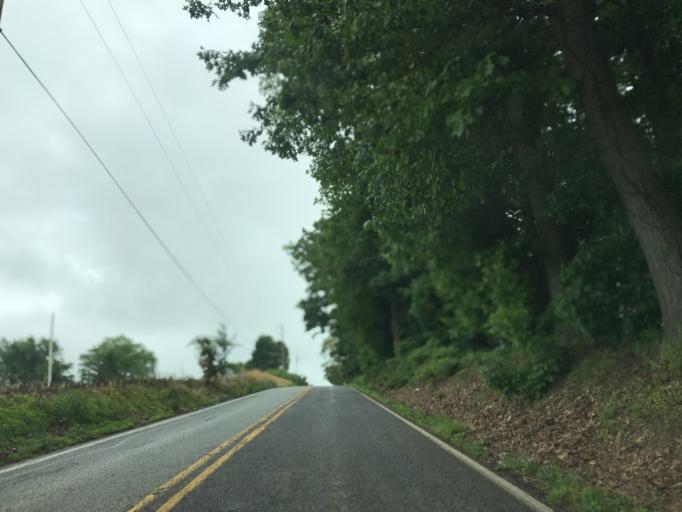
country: US
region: Pennsylvania
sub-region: York County
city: Susquehanna Trails
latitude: 39.7399
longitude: -76.4527
